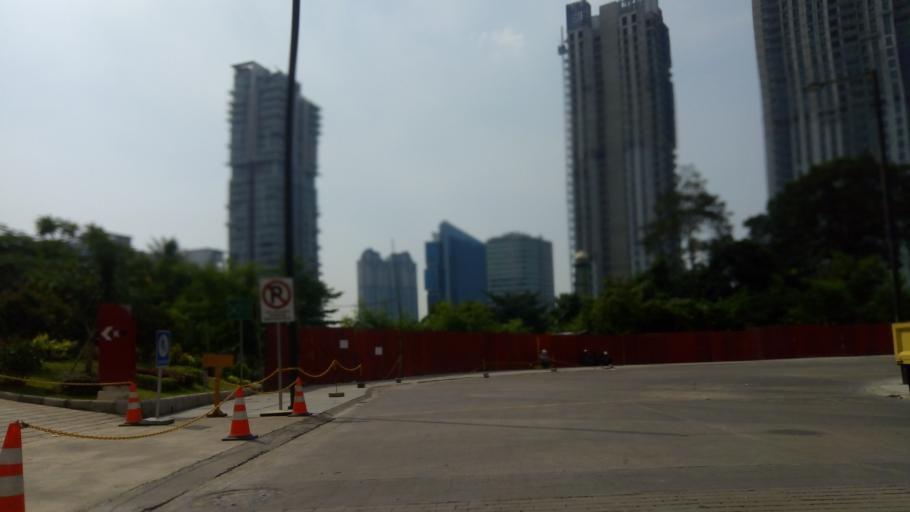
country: ID
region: Jakarta Raya
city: Jakarta
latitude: -6.2176
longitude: 106.8336
